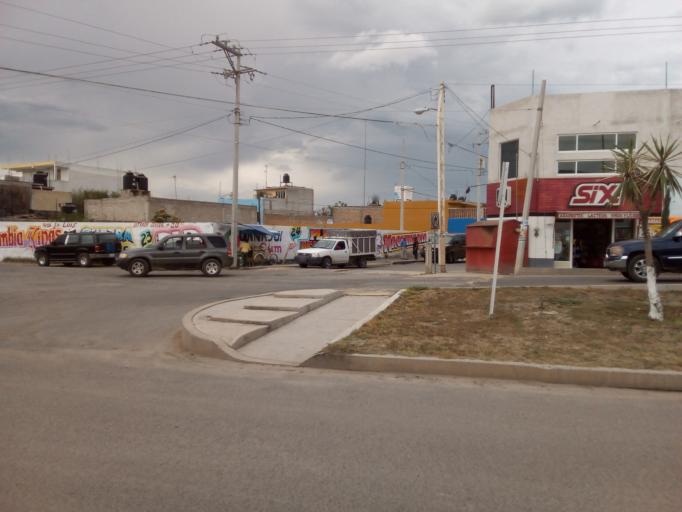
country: MX
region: Guerrero
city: San Luis de la Paz
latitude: 21.2878
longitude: -100.5236
